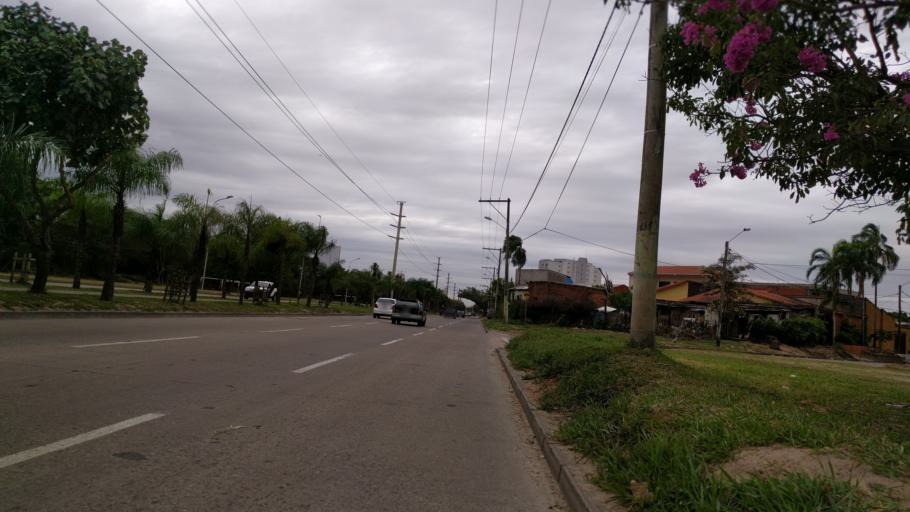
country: BO
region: Santa Cruz
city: Santa Cruz de la Sierra
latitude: -17.7739
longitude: -63.2135
